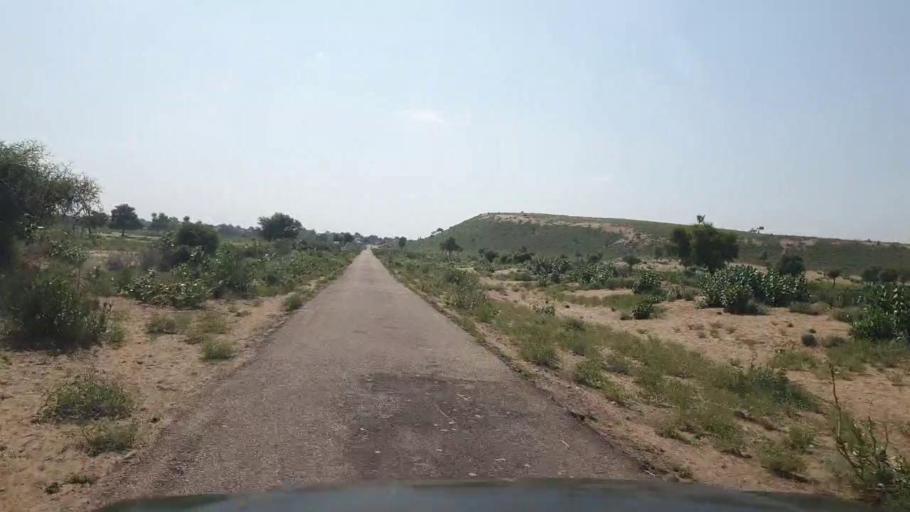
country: PK
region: Sindh
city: Islamkot
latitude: 25.1631
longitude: 70.4053
